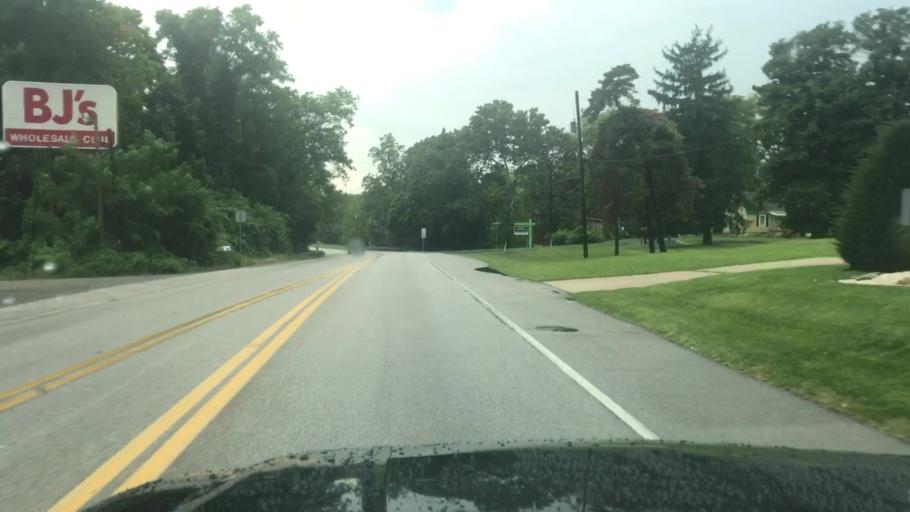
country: US
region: Pennsylvania
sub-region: Cumberland County
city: Shiremanstown
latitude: 40.2191
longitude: -76.9358
